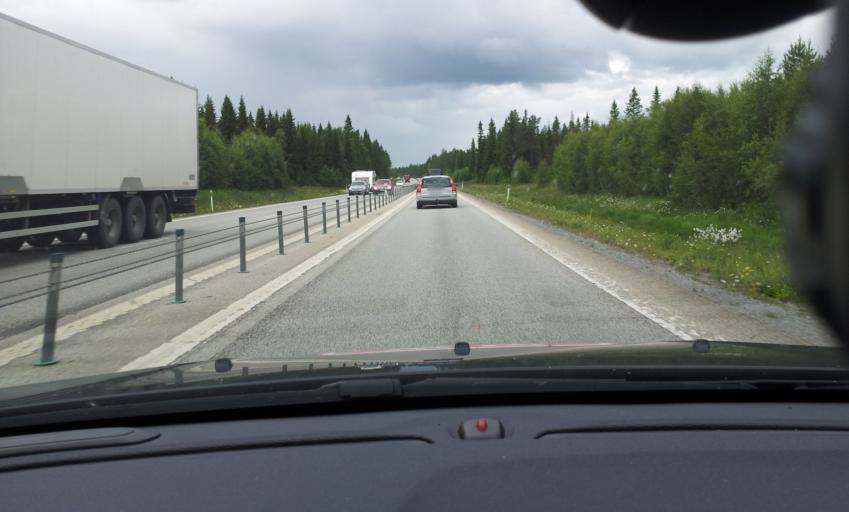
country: SE
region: Jaemtland
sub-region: OEstersunds Kommun
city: Brunflo
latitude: 63.1443
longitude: 14.7813
